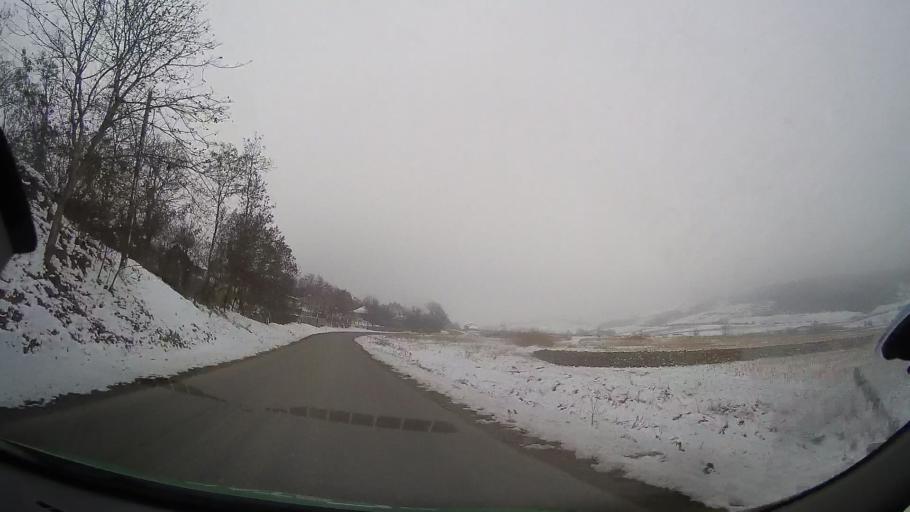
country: RO
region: Bacau
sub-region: Comuna Vultureni
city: Vultureni
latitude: 46.3525
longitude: 27.2885
